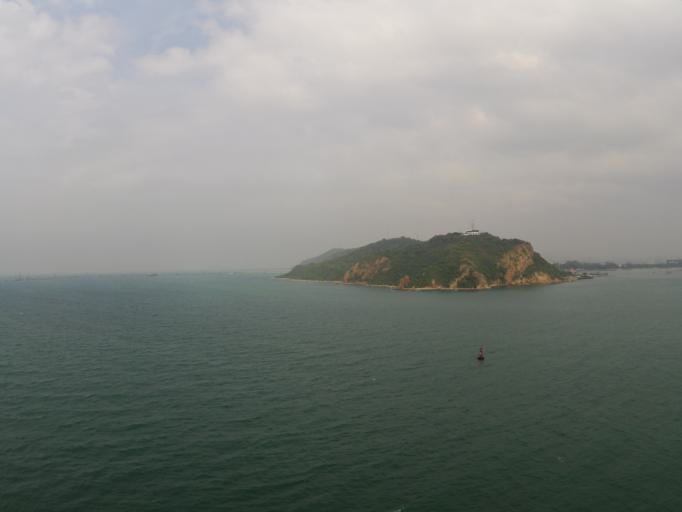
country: TH
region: Chon Buri
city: Bang Lamung
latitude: 13.0719
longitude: 100.8692
